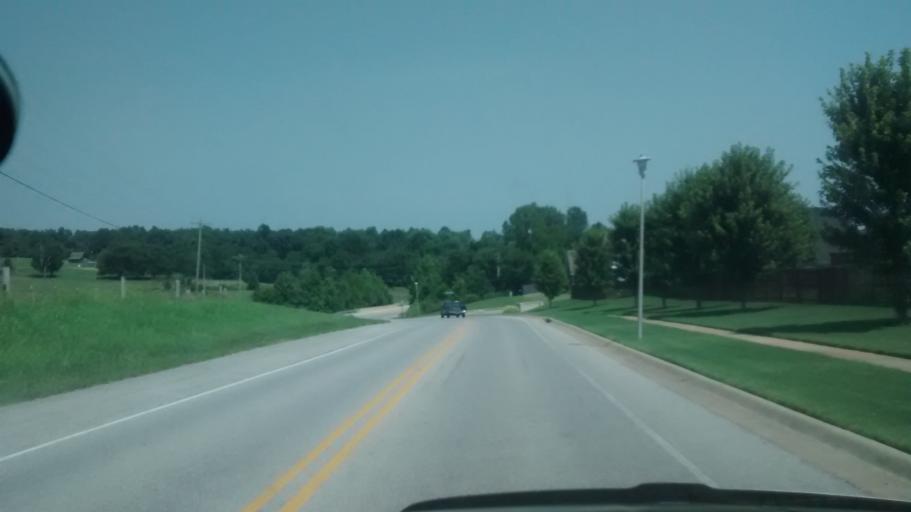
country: US
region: Arkansas
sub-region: Washington County
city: Farmington
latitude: 36.0721
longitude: -94.2533
